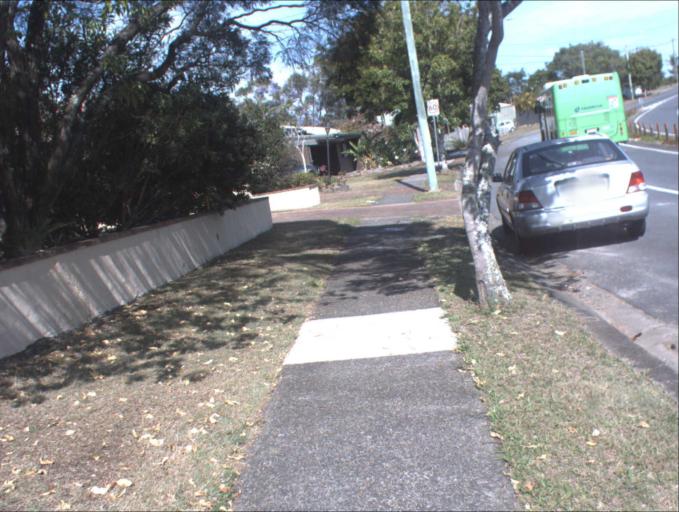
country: AU
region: Queensland
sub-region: Logan
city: Slacks Creek
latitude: -27.6505
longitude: 153.1770
